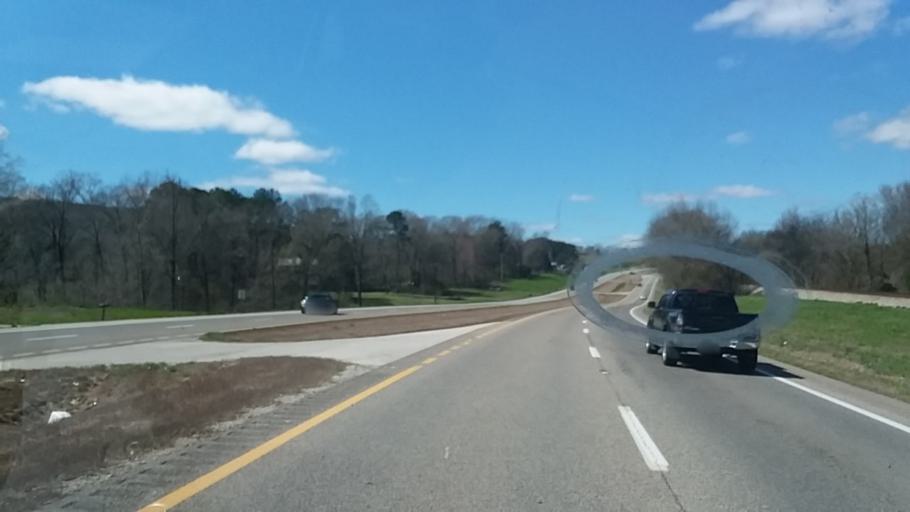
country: US
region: Alabama
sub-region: Colbert County
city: Tuscumbia
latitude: 34.7104
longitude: -87.7697
